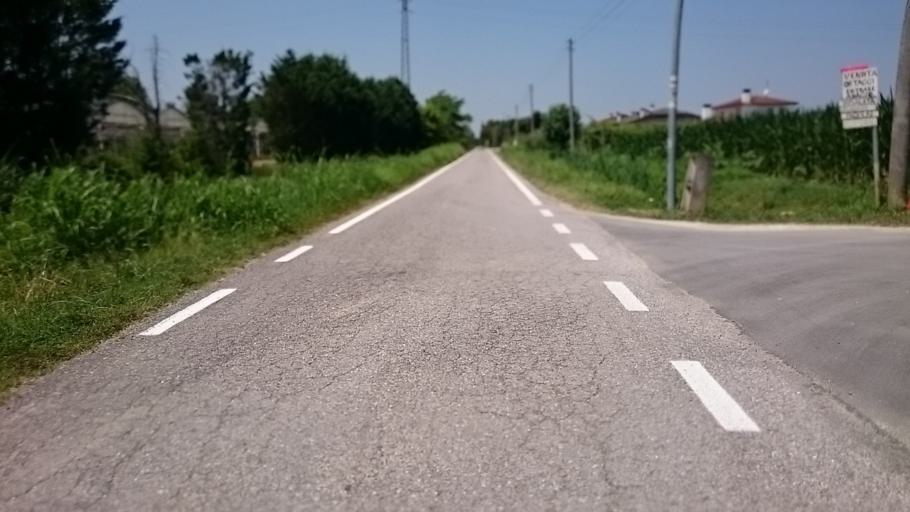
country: IT
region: Veneto
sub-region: Provincia di Padova
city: Villanova
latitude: 45.5095
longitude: 11.9907
